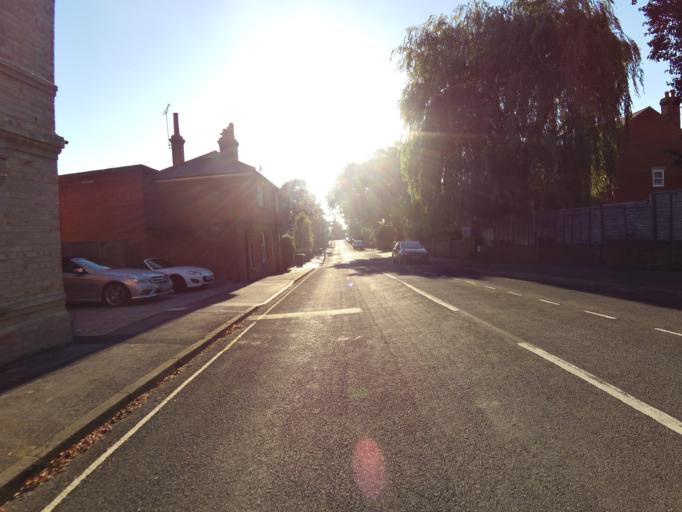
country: GB
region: England
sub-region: Suffolk
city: Ipswich
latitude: 52.0643
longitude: 1.1472
